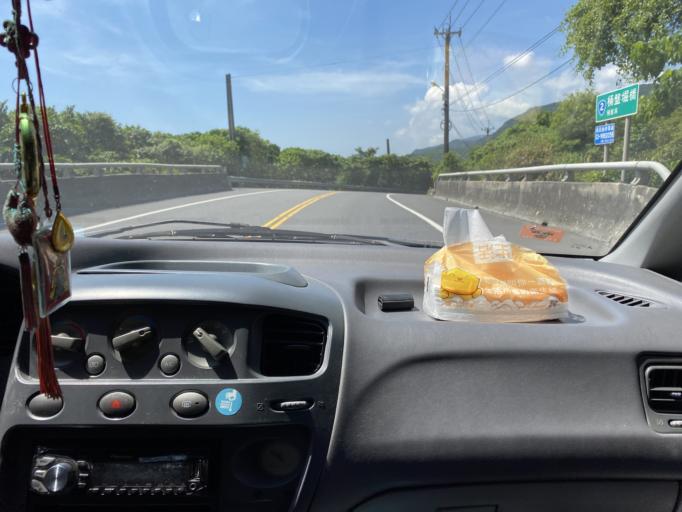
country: TW
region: Taiwan
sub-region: Keelung
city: Keelung
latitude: 24.9742
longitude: 121.9343
